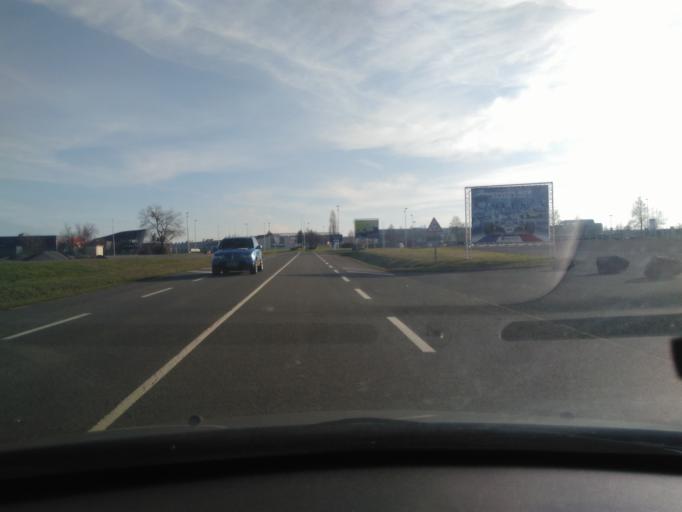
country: FR
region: Bourgogne
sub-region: Departement de la Nievre
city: Magny-Cours
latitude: 46.8685
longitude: 3.1584
